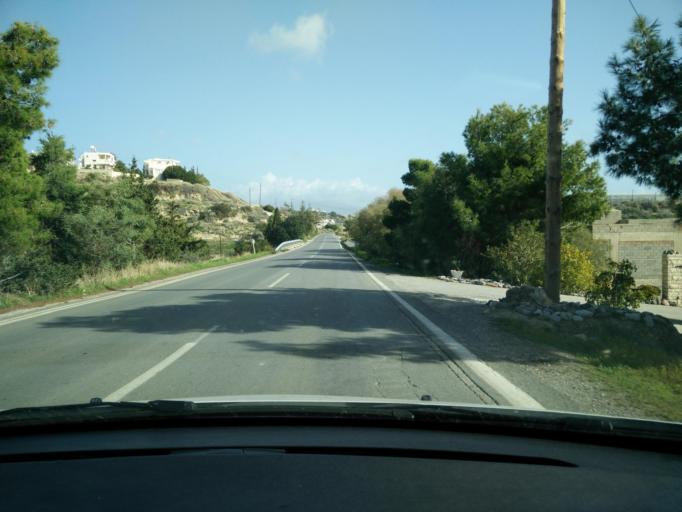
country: GR
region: Crete
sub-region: Nomos Lasithiou
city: Gra Liyia
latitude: 35.0082
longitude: 25.6390
